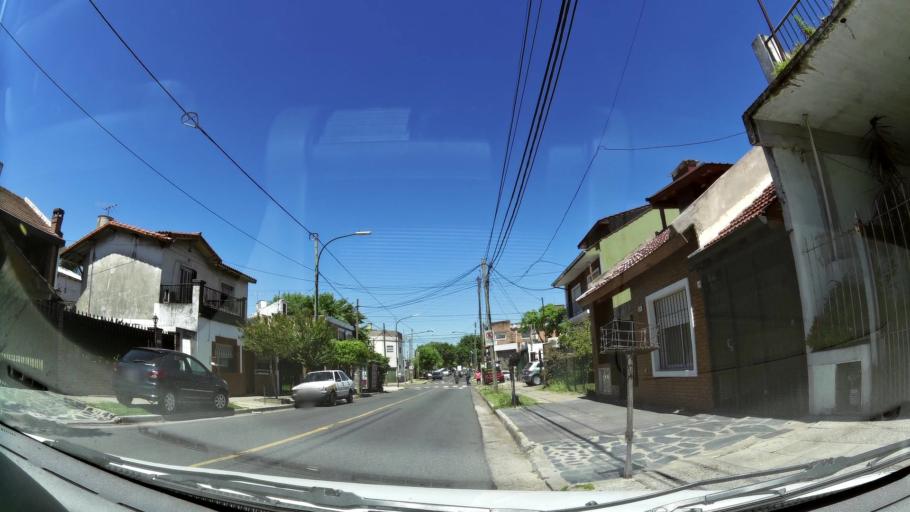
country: AR
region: Buenos Aires
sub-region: Partido de San Isidro
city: San Isidro
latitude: -34.5079
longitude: -58.5538
